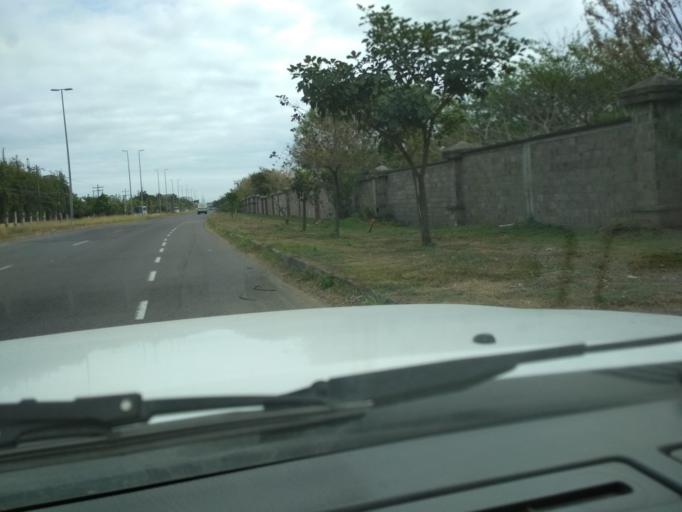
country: MX
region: Veracruz
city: Boca del Rio
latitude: 19.0896
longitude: -96.1164
